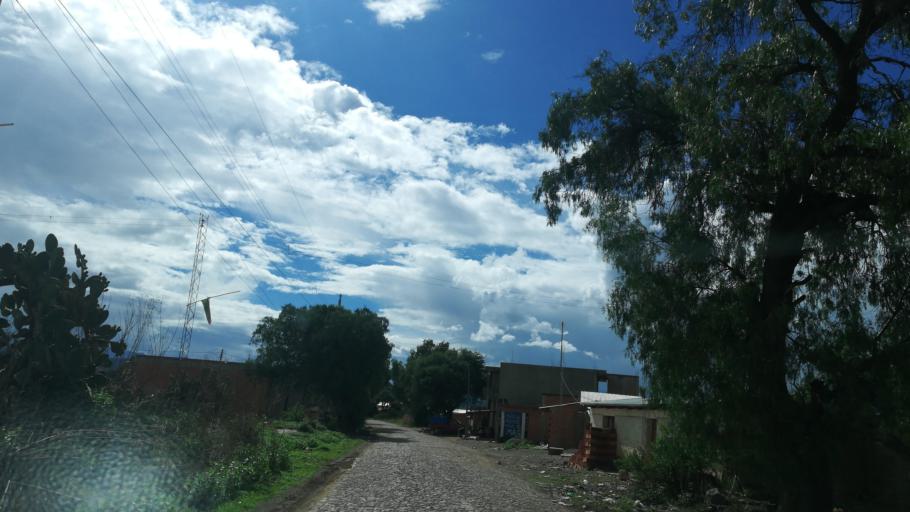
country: BO
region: Cochabamba
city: Capinota
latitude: -17.5494
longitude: -66.2327
